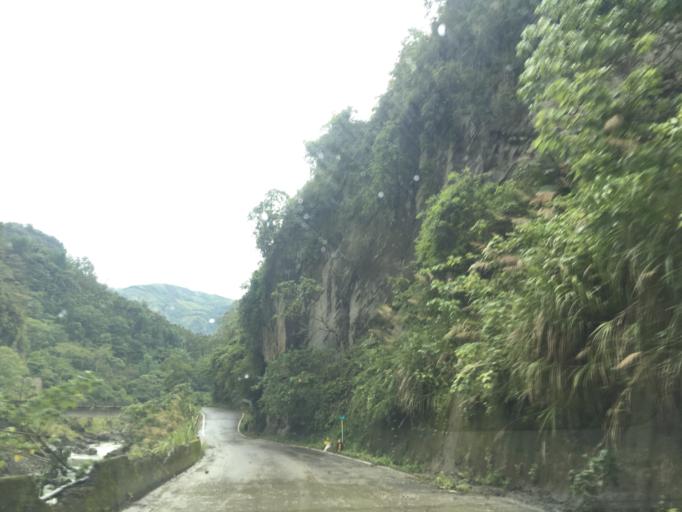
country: TW
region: Taiwan
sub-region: Yunlin
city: Douliu
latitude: 23.5657
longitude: 120.6406
